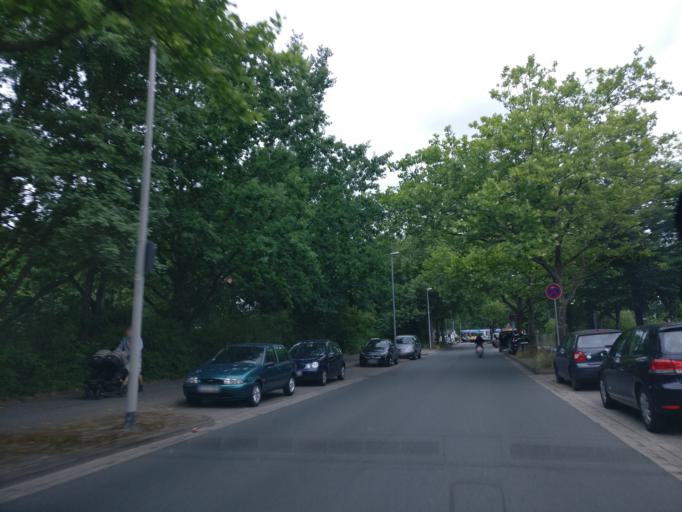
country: DE
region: Lower Saxony
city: Laatzen
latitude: 52.3369
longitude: 9.7733
